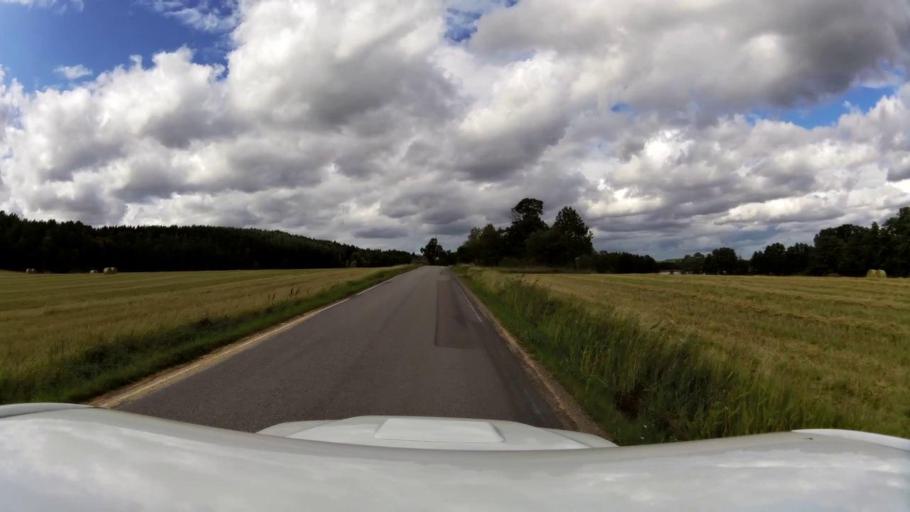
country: SE
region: OEstergoetland
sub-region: Linkopings Kommun
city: Sturefors
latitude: 58.3174
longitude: 15.7214
